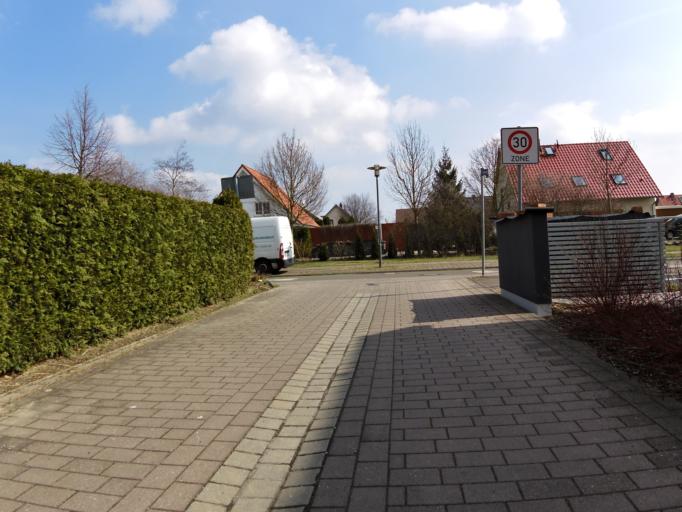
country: DE
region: Saxony
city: Markranstadt
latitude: 51.3064
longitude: 12.2947
